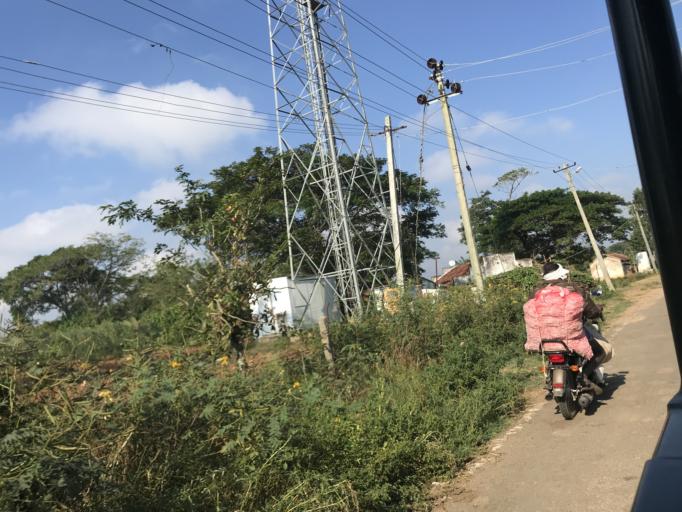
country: IN
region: Karnataka
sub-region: Mysore
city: Sargur
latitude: 11.9439
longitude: 76.2669
